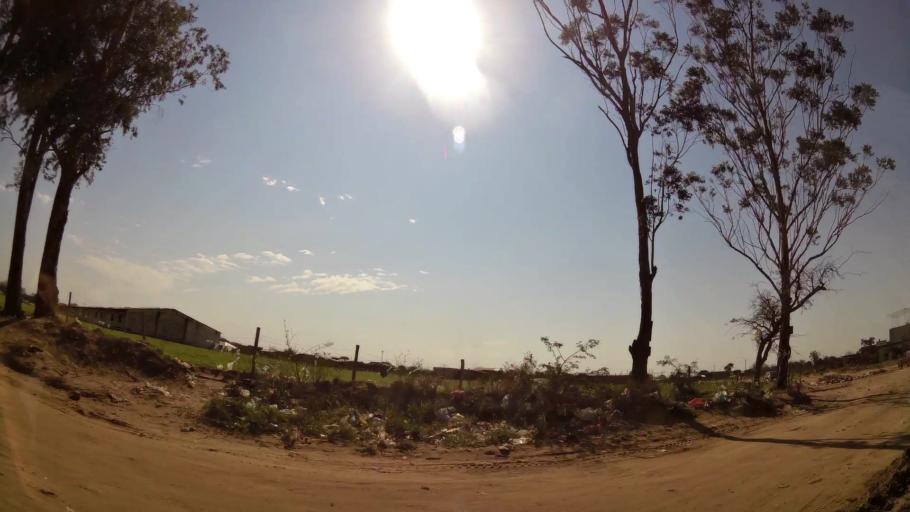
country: BO
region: Santa Cruz
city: Cotoca
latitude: -17.7467
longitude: -63.0820
